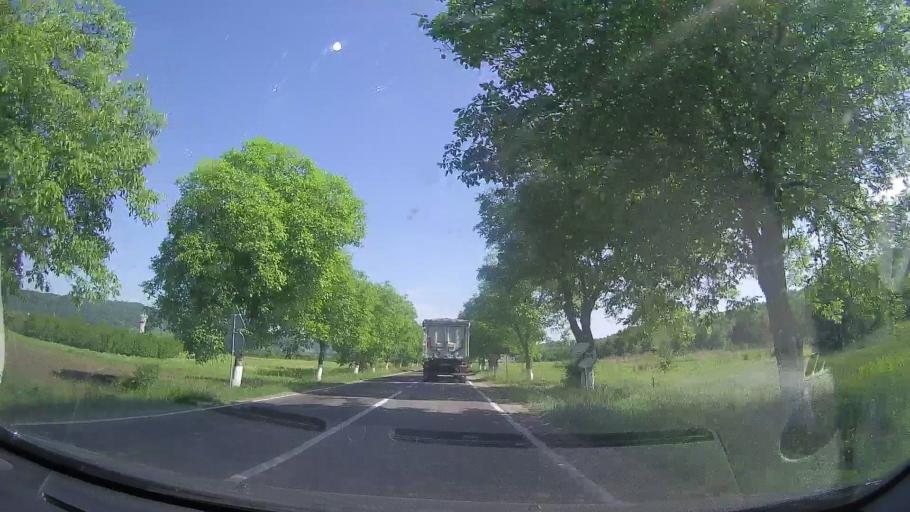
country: RO
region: Prahova
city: Drajna de Jos
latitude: 45.2268
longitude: 26.0304
